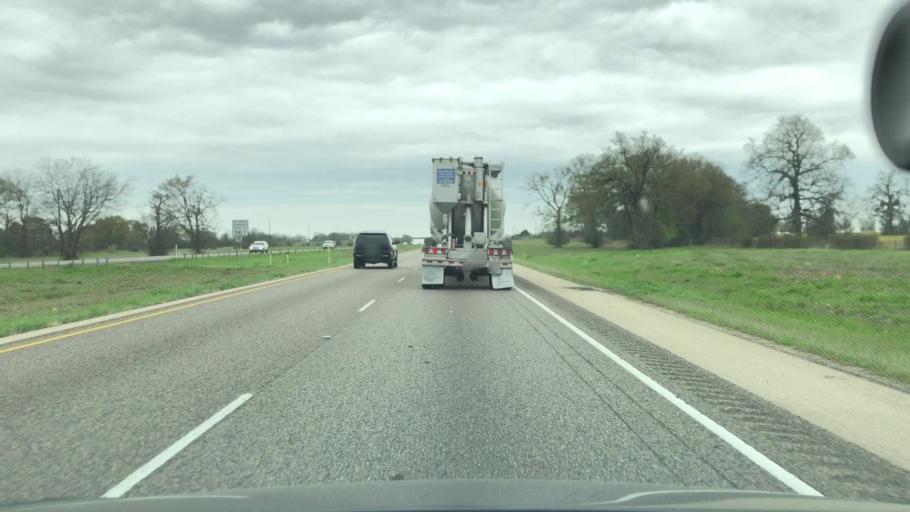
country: US
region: Texas
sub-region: Madison County
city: Madisonville
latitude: 31.0633
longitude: -95.9511
